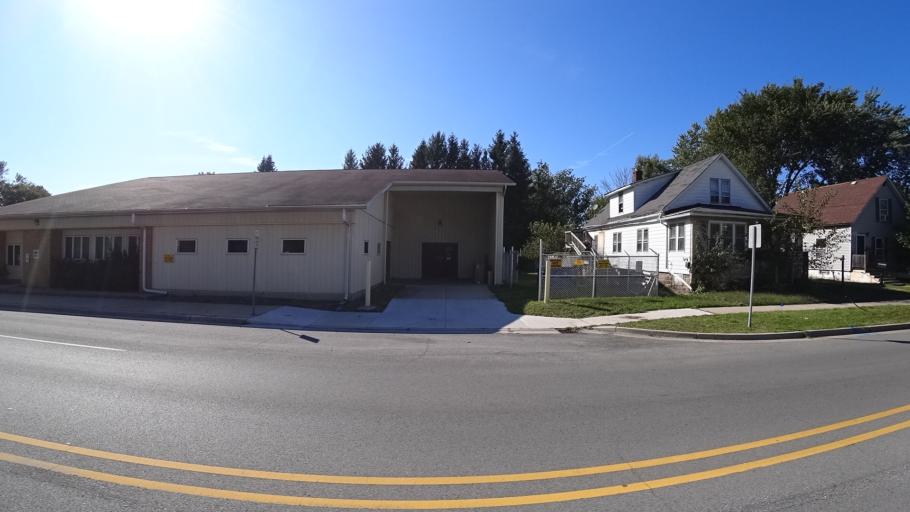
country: US
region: Indiana
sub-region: LaPorte County
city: Michigan City
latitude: 41.7009
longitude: -86.9038
